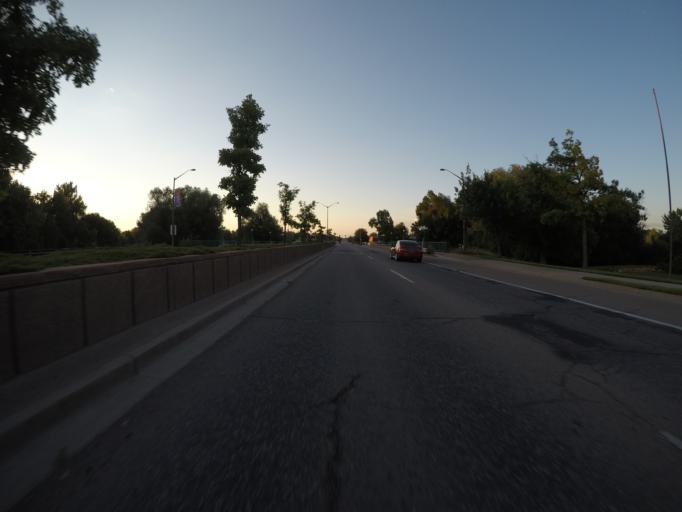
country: US
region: Colorado
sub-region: Larimer County
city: Fort Collins
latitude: 40.5946
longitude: -105.0767
